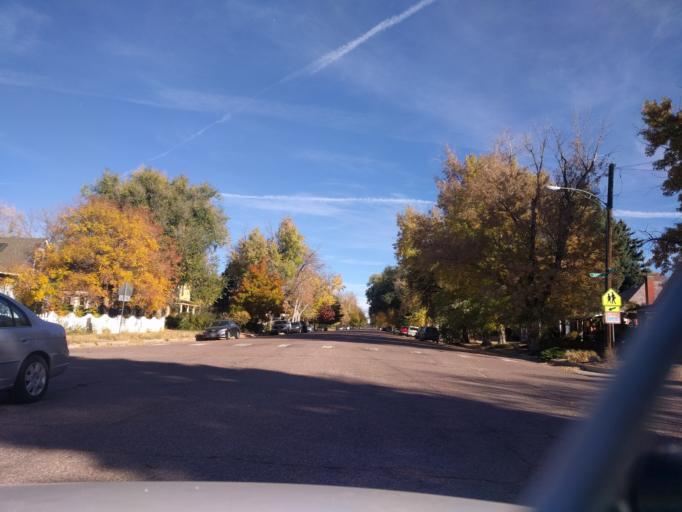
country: US
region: Colorado
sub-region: El Paso County
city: Colorado Springs
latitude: 38.8475
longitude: -104.8156
